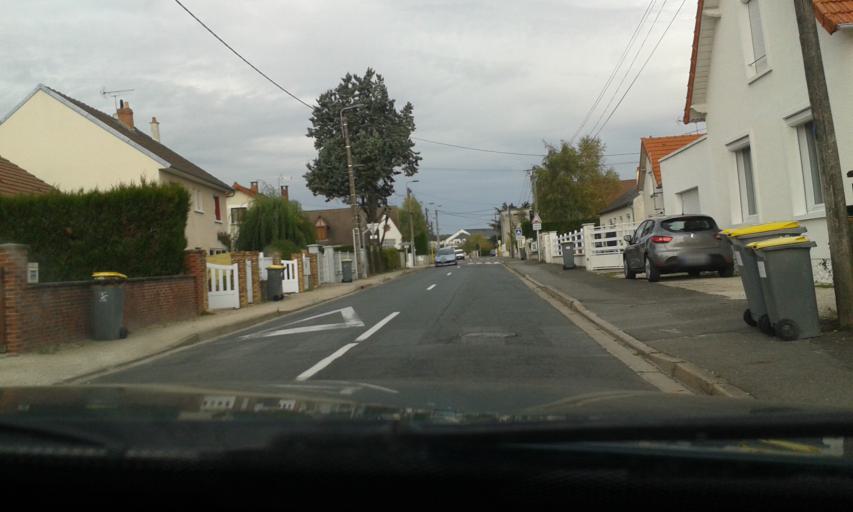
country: FR
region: Centre
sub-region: Departement du Loiret
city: Saran
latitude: 47.9479
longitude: 1.8821
